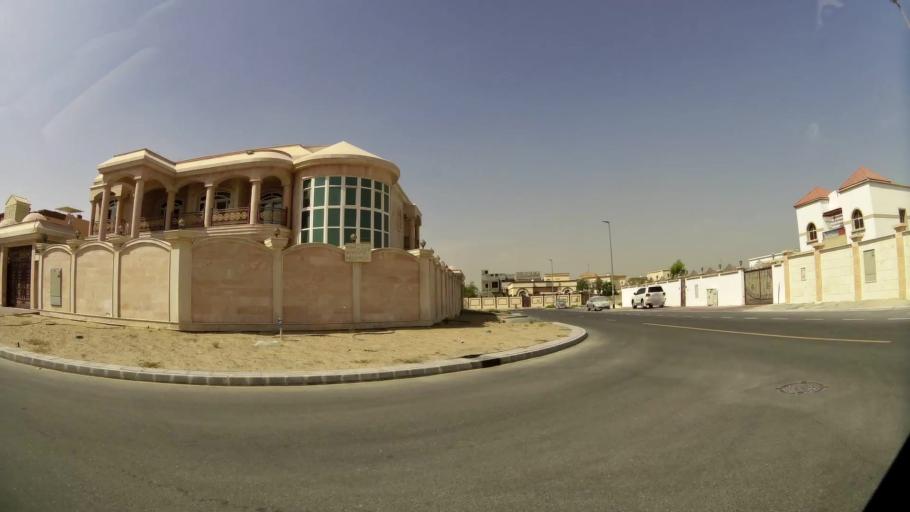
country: AE
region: Ash Shariqah
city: Sharjah
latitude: 25.2002
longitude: 55.4152
